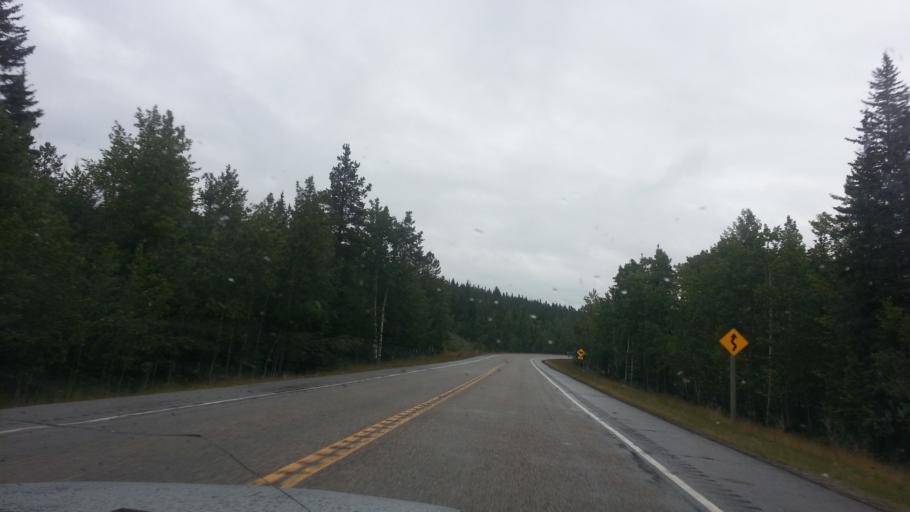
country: CA
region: Alberta
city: Cochrane
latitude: 50.8760
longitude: -114.7195
